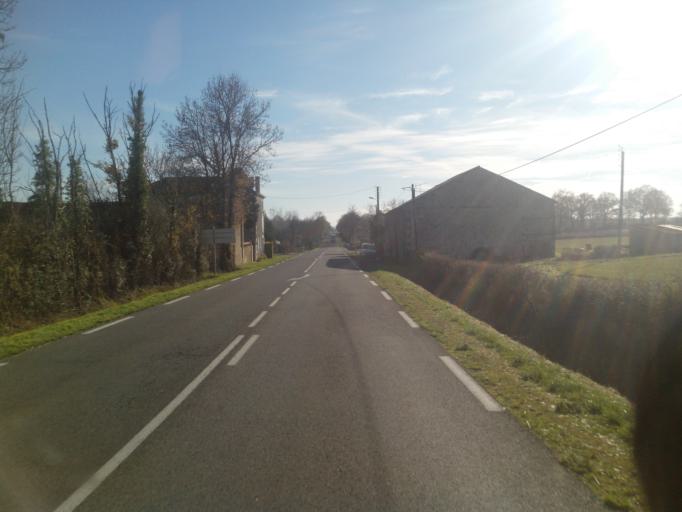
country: FR
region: Limousin
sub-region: Departement de la Haute-Vienne
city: Bussiere-Poitevine
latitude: 46.2300
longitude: 0.8984
